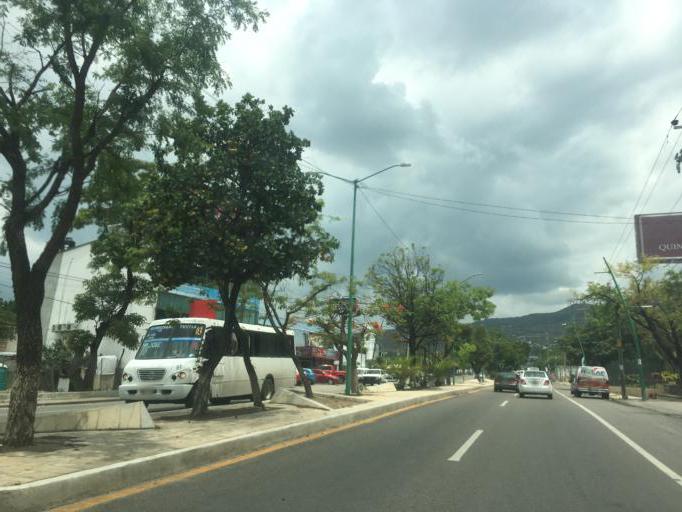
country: MX
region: Chiapas
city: Tuxtla Gutierrez
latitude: 16.7530
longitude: -93.1420
